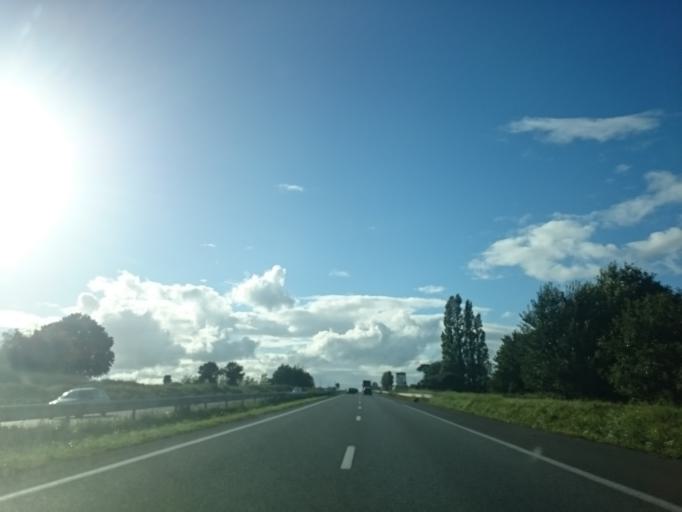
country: FR
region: Brittany
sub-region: Departement des Cotes-d'Armor
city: Saint-Agathon
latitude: 48.5482
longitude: -3.1018
